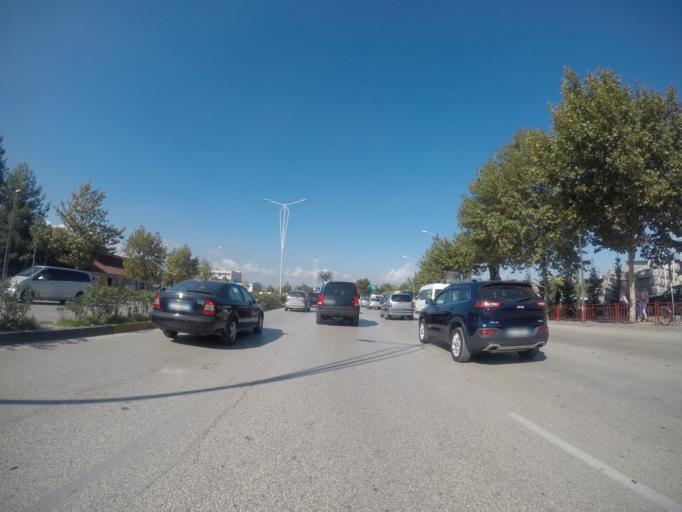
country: AL
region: Tirane
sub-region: Rrethi i Tiranes
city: Paskuqan
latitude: 41.3389
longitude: 19.7876
